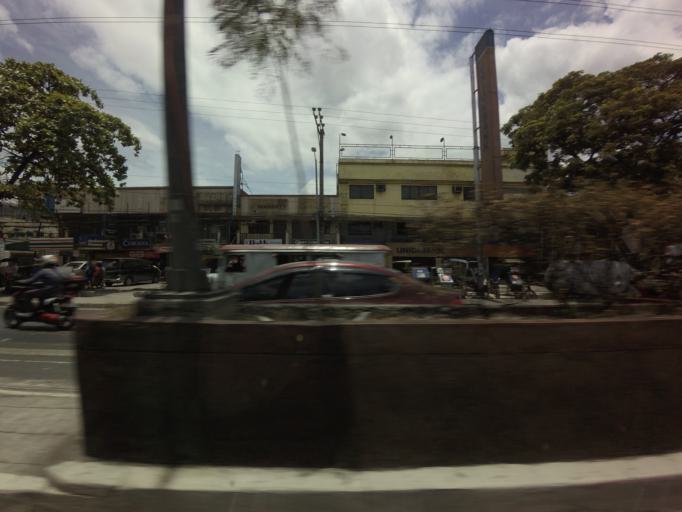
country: PH
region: Metro Manila
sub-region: Marikina
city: Calumpang
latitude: 14.6101
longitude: 121.1037
